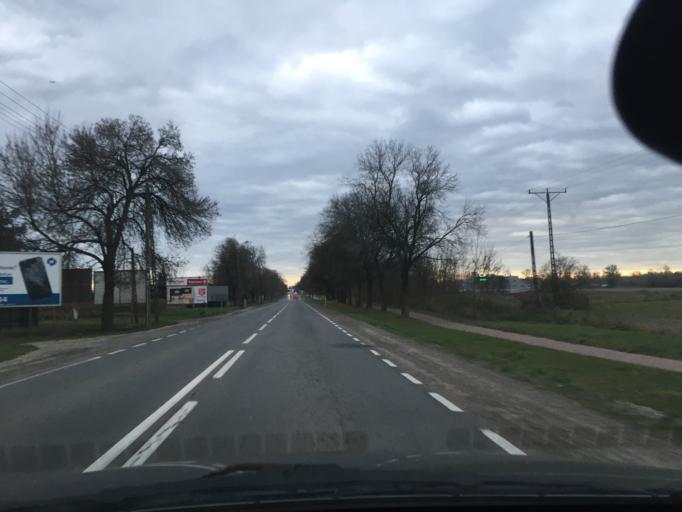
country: PL
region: Masovian Voivodeship
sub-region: Powiat piaseczynski
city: Lesznowola
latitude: 52.0943
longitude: 20.9270
